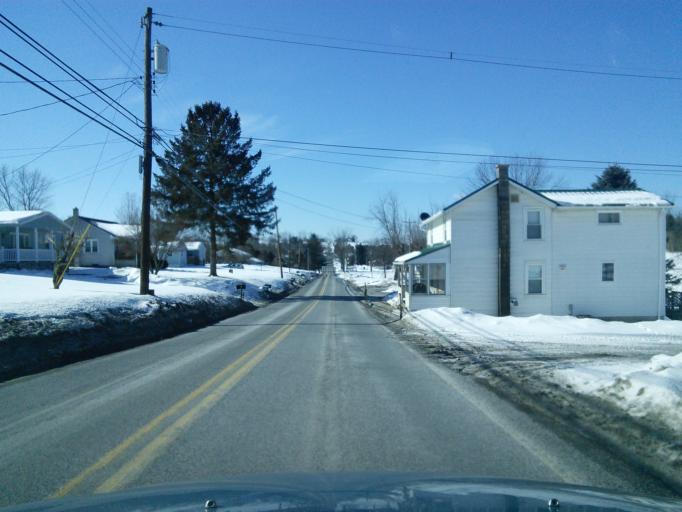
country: US
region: Pennsylvania
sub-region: Centre County
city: Houserville
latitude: 40.8811
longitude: -77.8380
